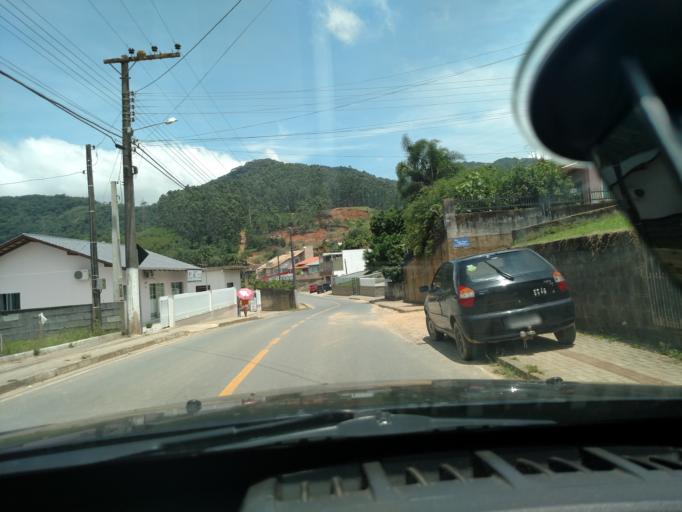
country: BR
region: Santa Catarina
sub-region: Gaspar
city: Gaspar
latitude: -26.9103
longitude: -48.8184
